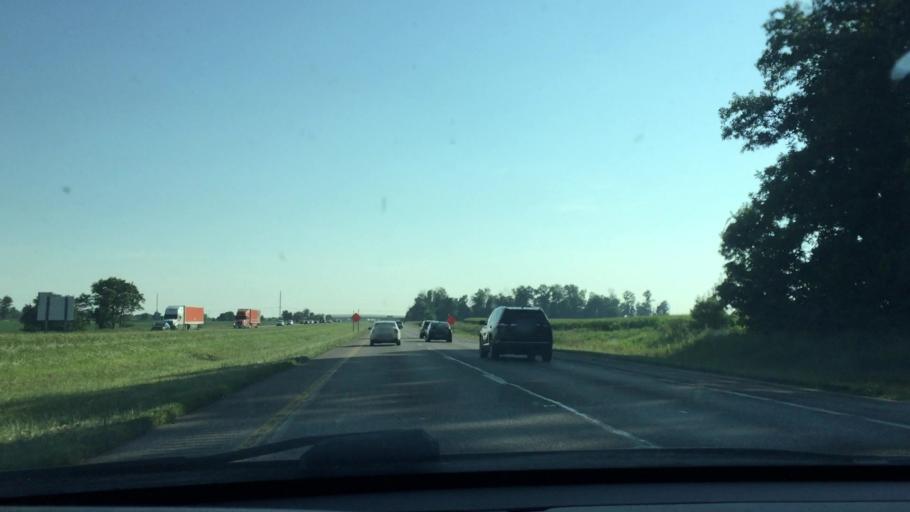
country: US
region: Ohio
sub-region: Warren County
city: Waynesville
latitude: 39.4693
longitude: -83.9758
